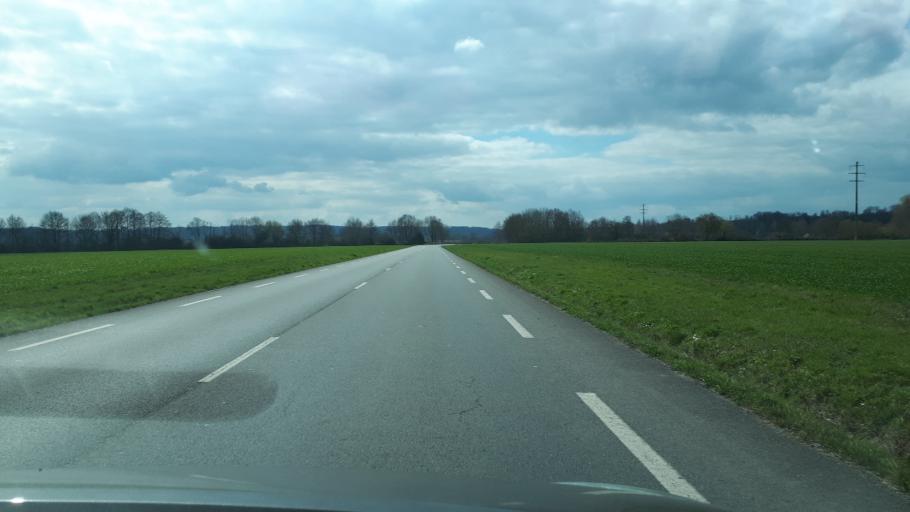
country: FR
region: Centre
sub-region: Departement du Loir-et-Cher
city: Lunay
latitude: 47.7672
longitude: 0.9064
